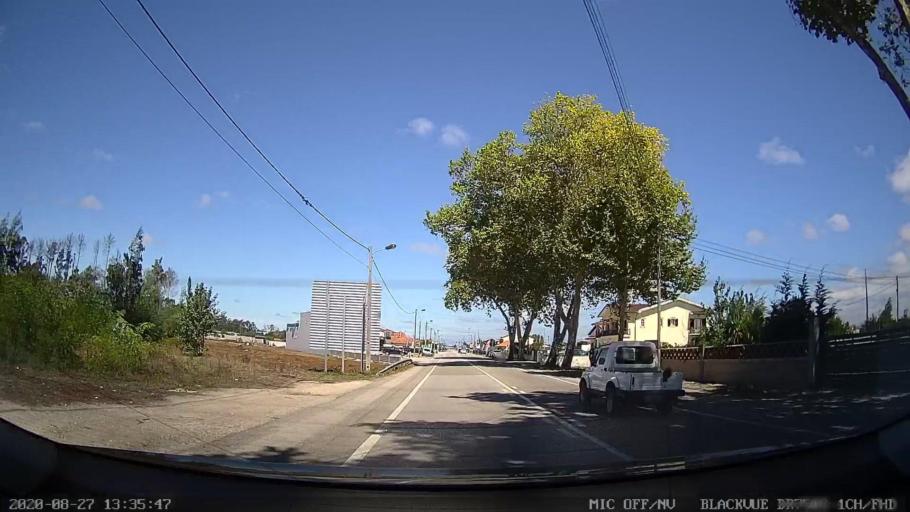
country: PT
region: Coimbra
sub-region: Mira
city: Mira
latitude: 40.4605
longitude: -8.7017
